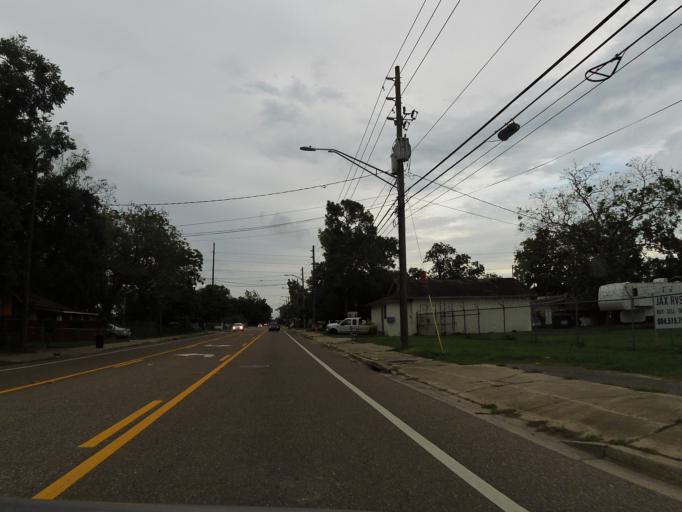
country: US
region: Florida
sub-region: Duval County
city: Jacksonville
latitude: 30.3219
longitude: -81.7151
